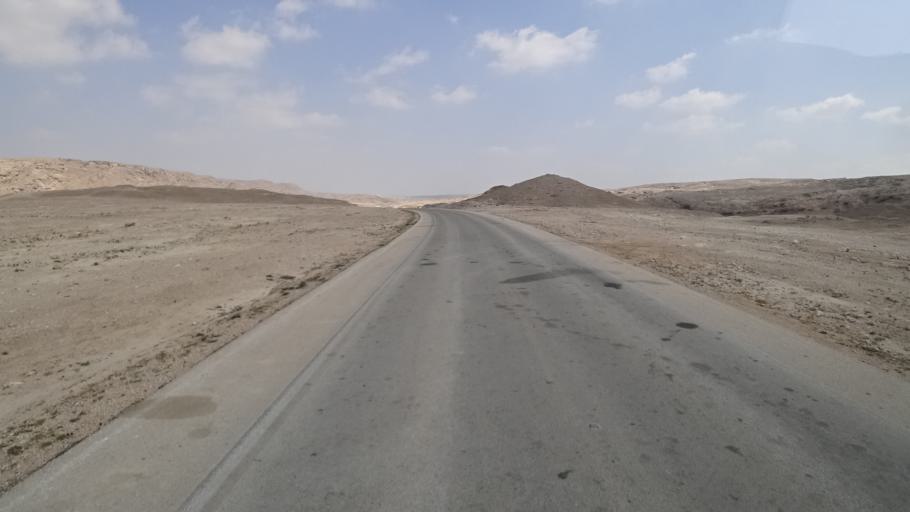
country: OM
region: Zufar
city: Salalah
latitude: 17.2495
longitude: 53.9632
